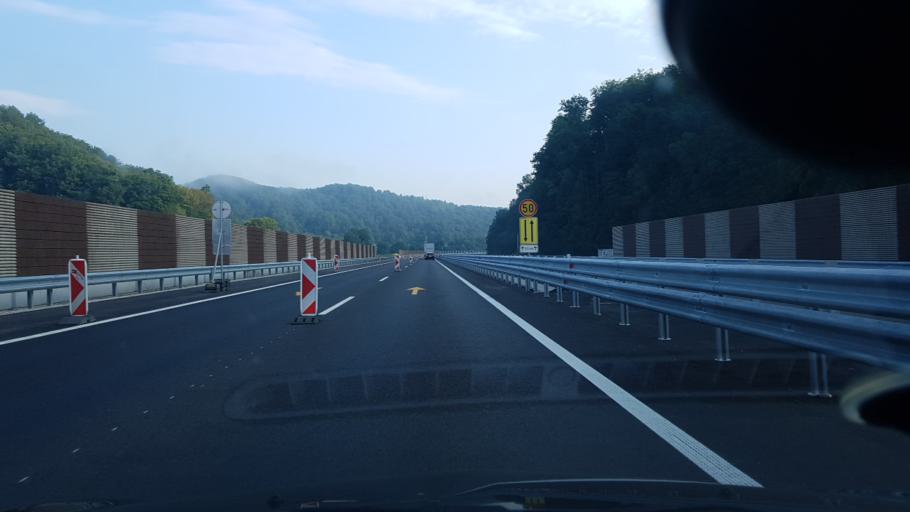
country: SI
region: Zetale
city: Zetale
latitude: 46.2942
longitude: 15.8555
